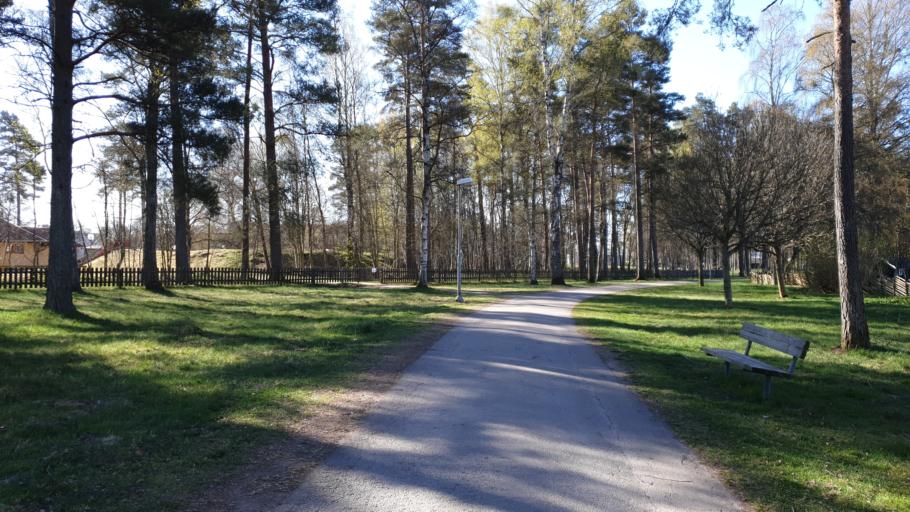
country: SE
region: Kronoberg
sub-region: Ljungby Kommun
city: Ljungby
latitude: 56.8335
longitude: 13.9149
